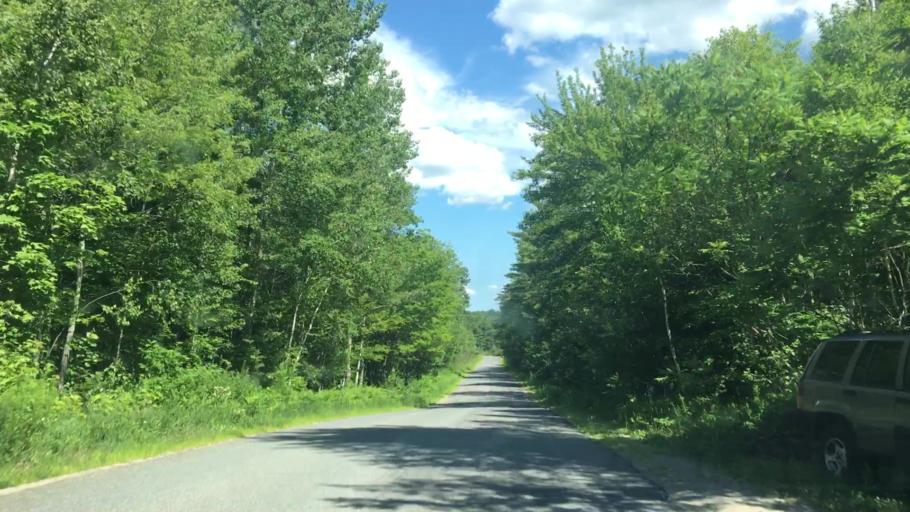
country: US
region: Maine
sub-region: Franklin County
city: Chesterville
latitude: 44.5535
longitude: -70.1019
